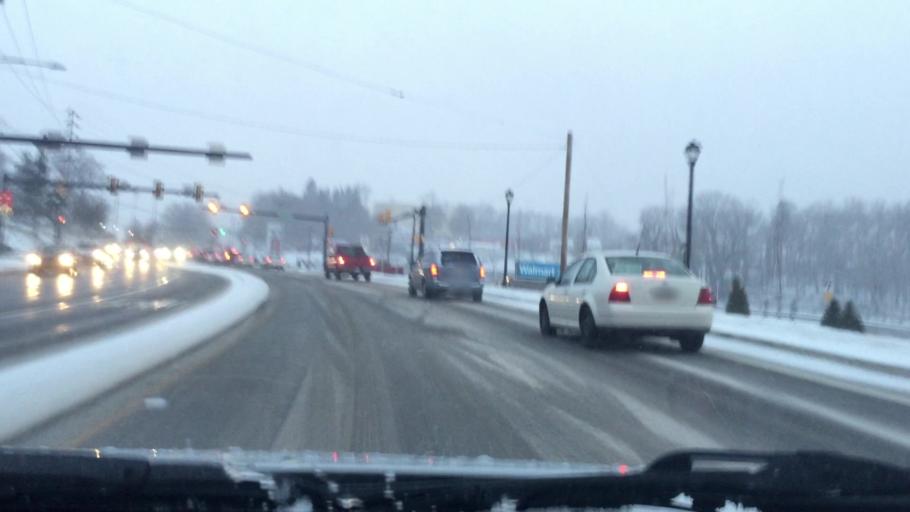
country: US
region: Pennsylvania
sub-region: Allegheny County
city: Carnot-Moon
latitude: 40.5158
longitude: -80.2223
